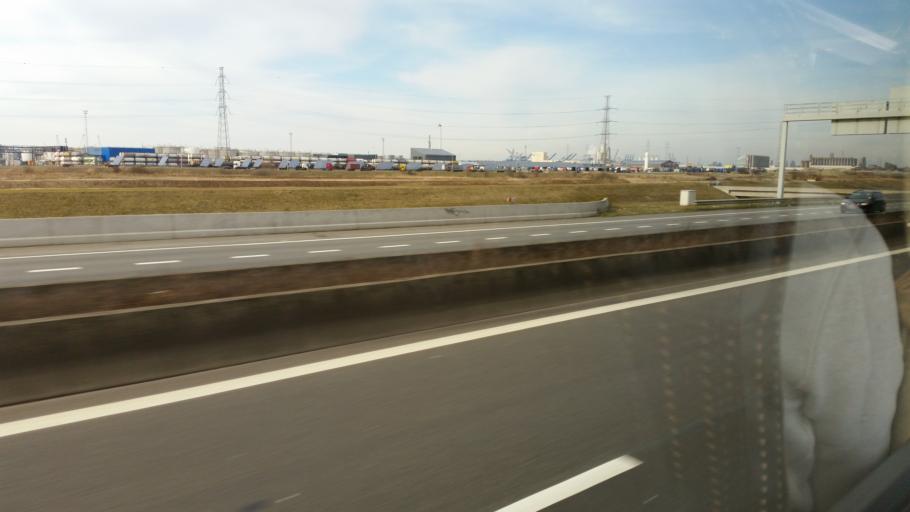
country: BE
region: Flanders
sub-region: Provincie Oost-Vlaanderen
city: Beveren
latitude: 51.2537
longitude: 4.2634
